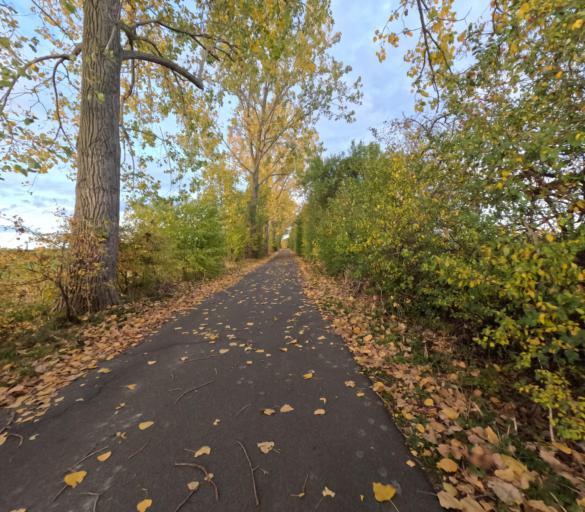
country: DE
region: Saxony
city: Grimma
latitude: 51.2453
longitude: 12.6935
